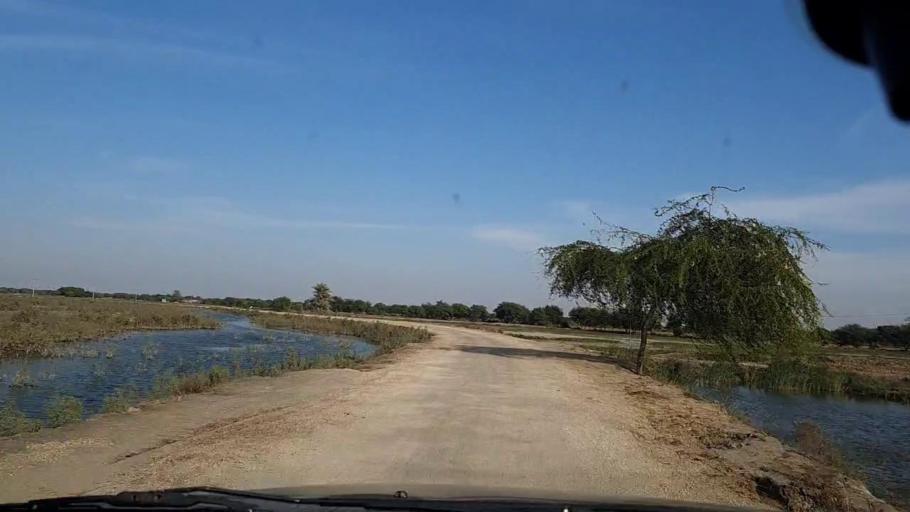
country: PK
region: Sindh
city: Mirpur Batoro
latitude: 24.6320
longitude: 68.2965
